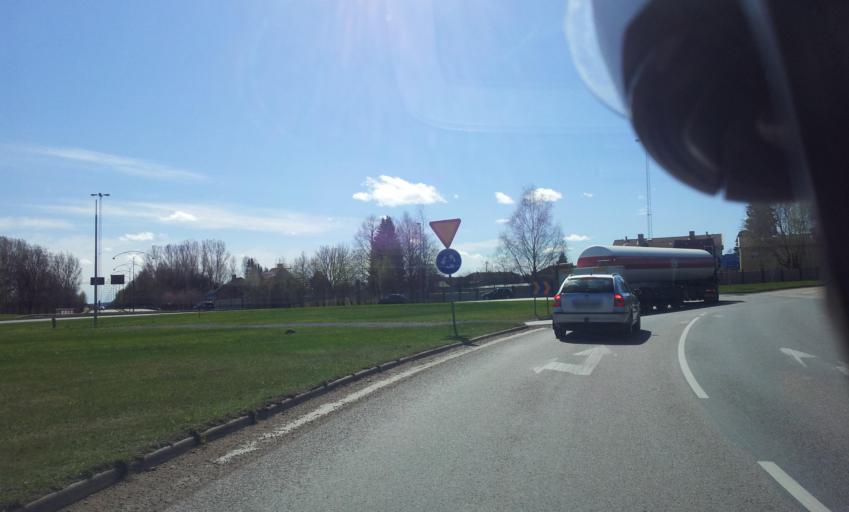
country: SE
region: Dalarna
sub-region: Borlange Kommun
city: Borlaenge
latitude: 60.4820
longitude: 15.4457
